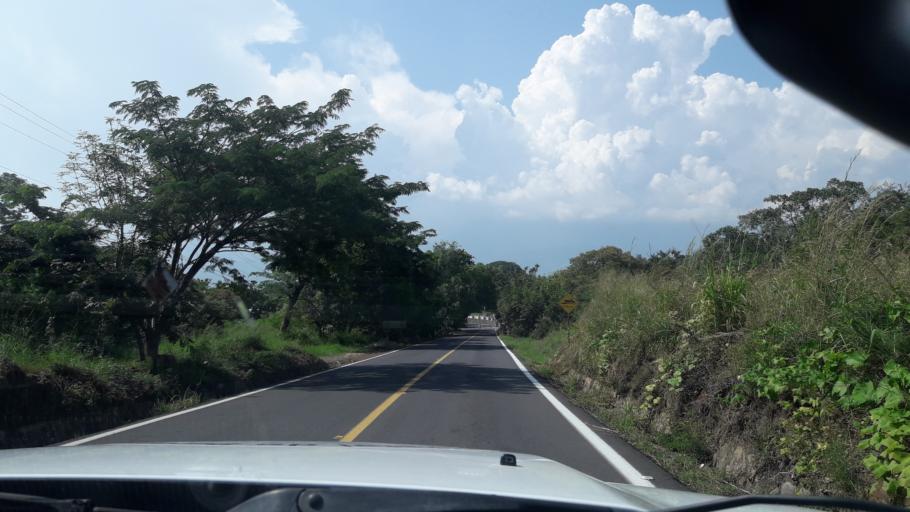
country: MX
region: Colima
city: Comala
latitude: 19.3314
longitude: -103.7501
